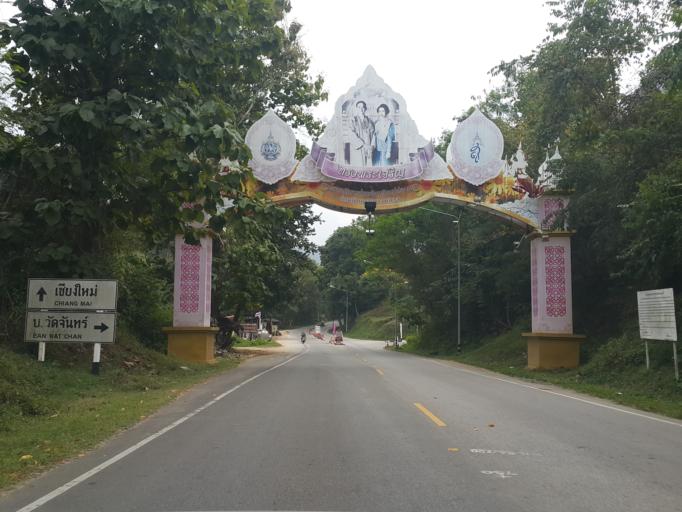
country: TH
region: Mae Hong Son
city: Mae Hi
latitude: 19.2861
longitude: 98.4824
